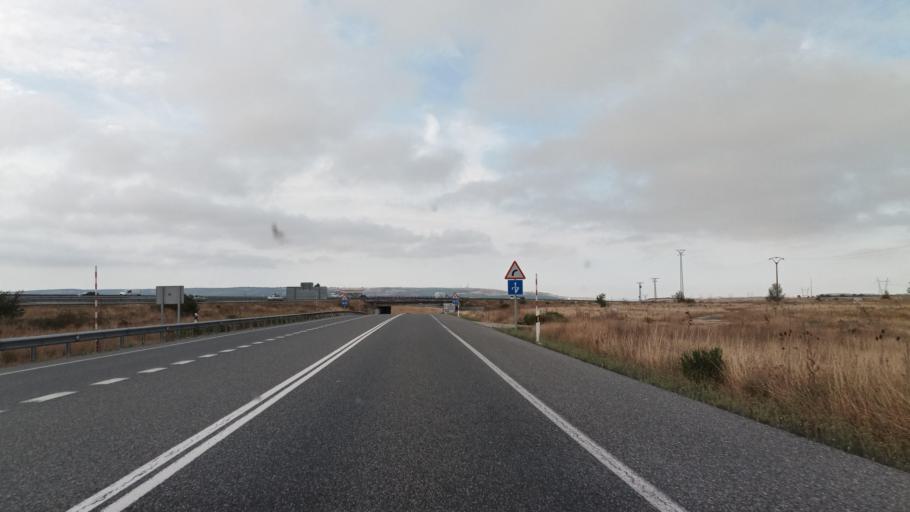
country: ES
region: Castille and Leon
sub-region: Provincia de Burgos
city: Fresno de Rodilla
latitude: 42.4271
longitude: -3.5063
